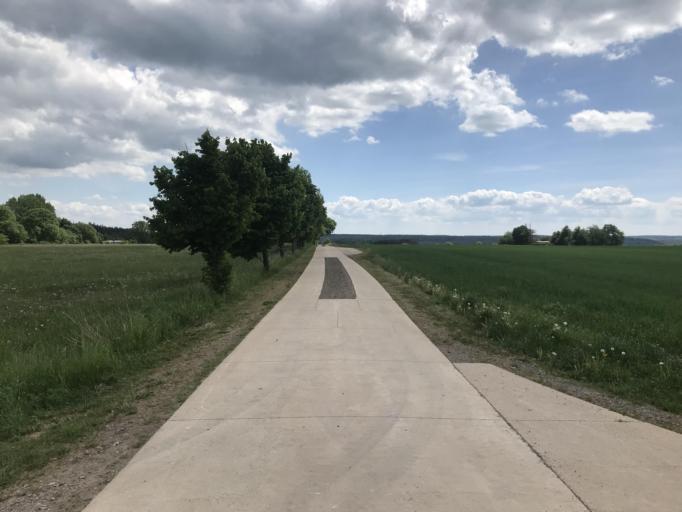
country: DE
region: Saxony-Anhalt
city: Harzgerode
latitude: 51.5934
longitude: 11.1513
